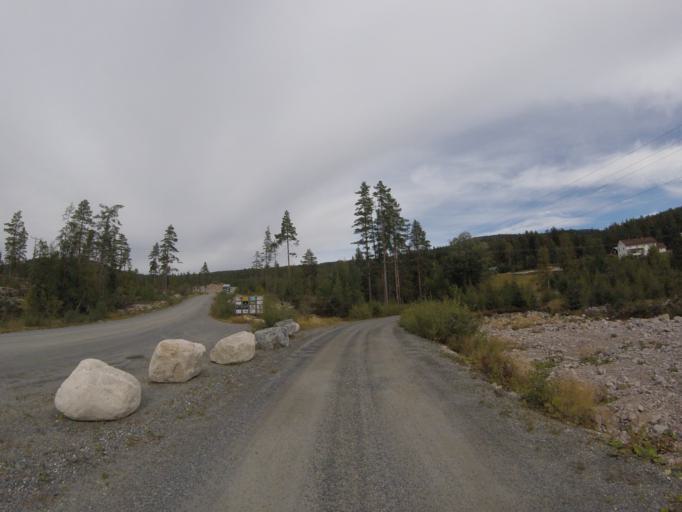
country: NO
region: Buskerud
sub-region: Flesberg
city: Lampeland
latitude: 59.7341
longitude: 9.3876
